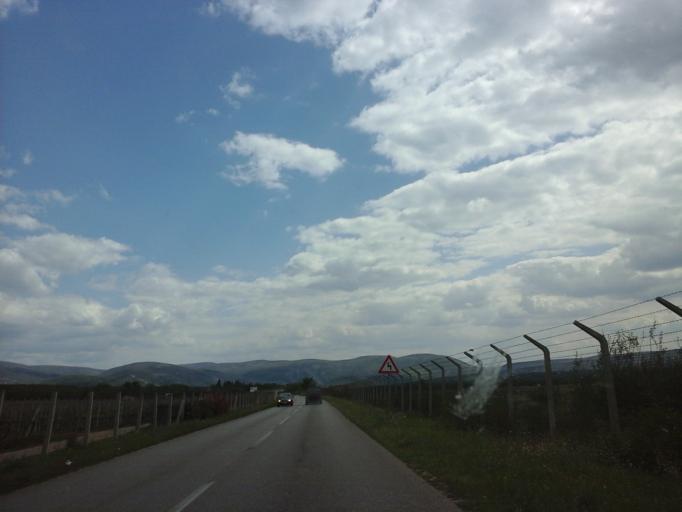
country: BA
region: Federation of Bosnia and Herzegovina
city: Blagaj
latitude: 43.2851
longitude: 17.8501
